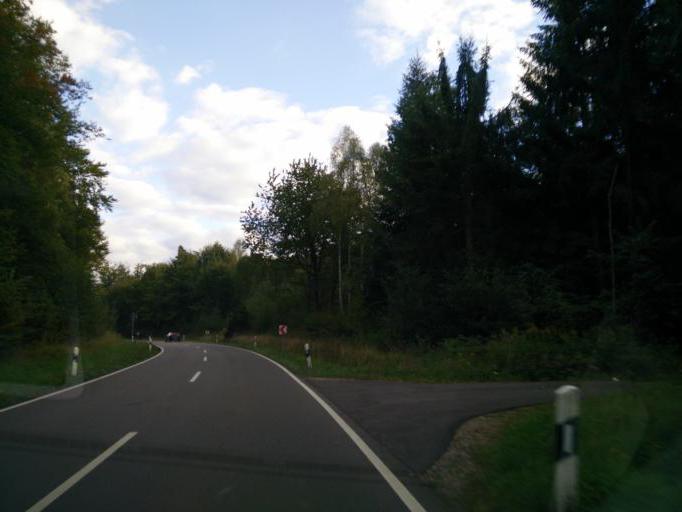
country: DE
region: Baden-Wuerttemberg
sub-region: Tuebingen Region
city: Dettenhausen
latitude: 48.5915
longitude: 9.0745
